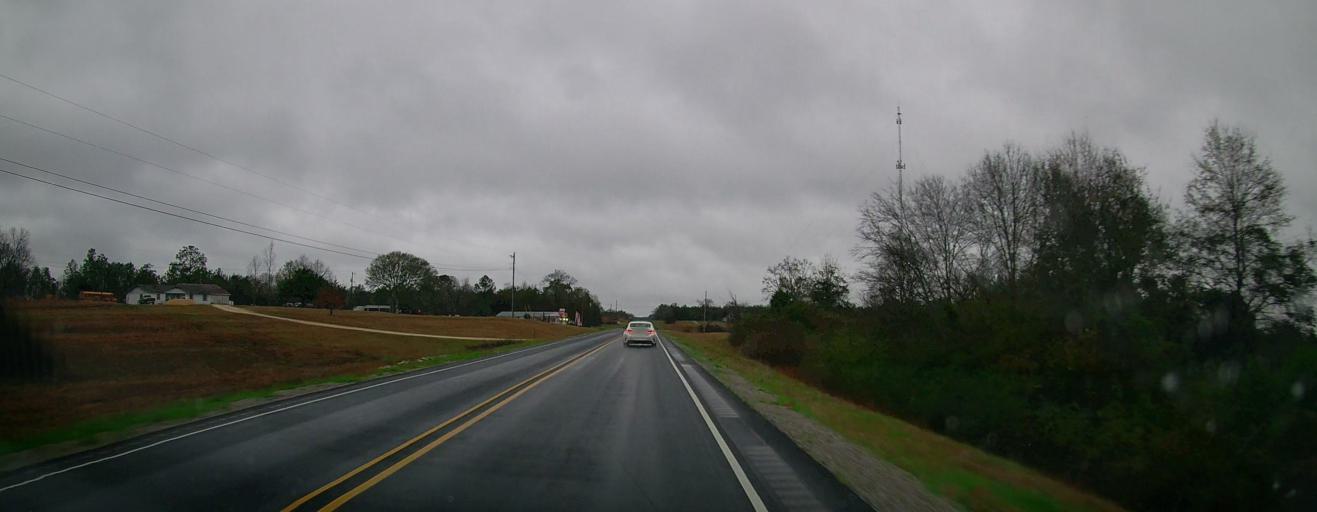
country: US
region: Alabama
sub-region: Chilton County
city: Clanton
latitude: 32.6515
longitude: -86.7659
